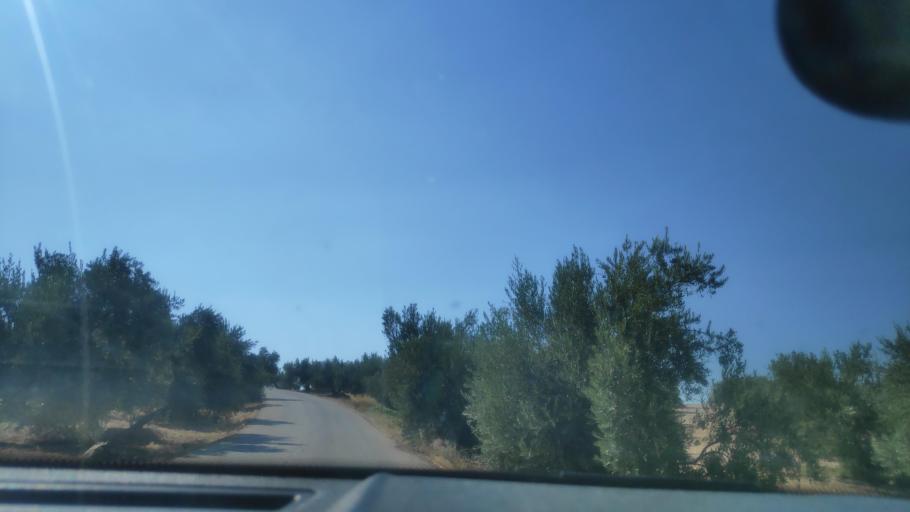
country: ES
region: Andalusia
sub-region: Provincia de Jaen
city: Jaen
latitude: 37.8291
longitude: -3.7605
